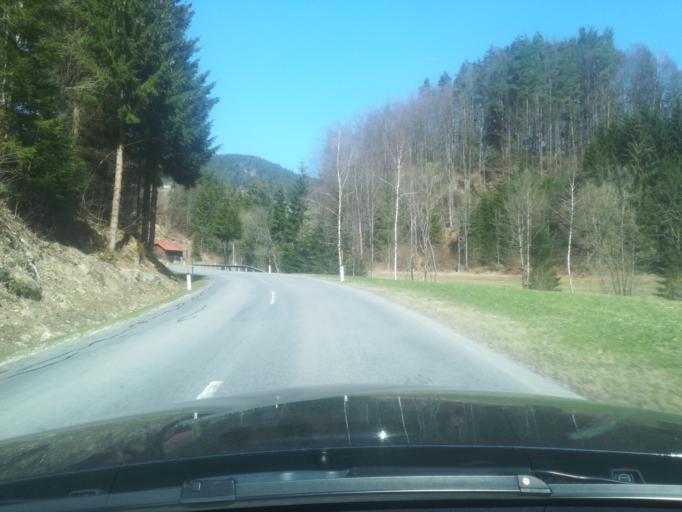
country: AT
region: Upper Austria
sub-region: Politischer Bezirk Perg
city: Sankt Georgen am Walde
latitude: 48.4501
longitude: 14.7854
